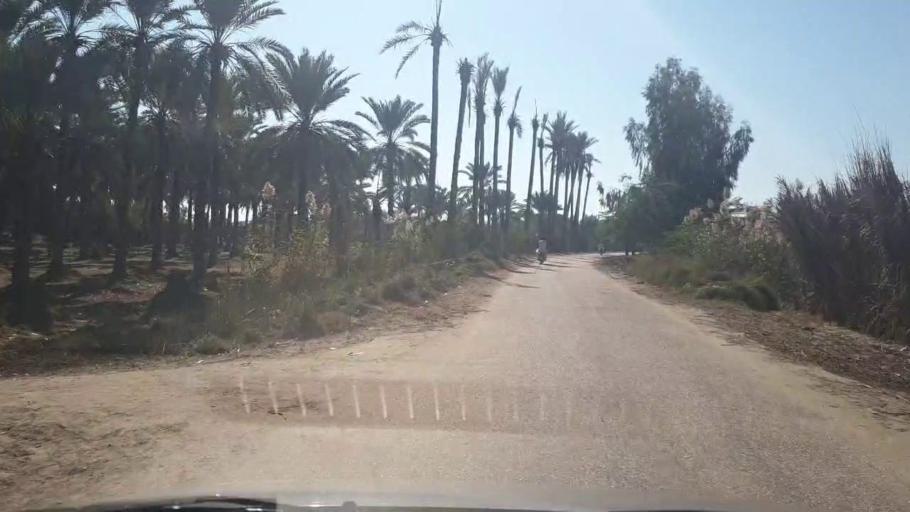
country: PK
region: Sindh
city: Bozdar
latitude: 27.1387
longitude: 68.6450
